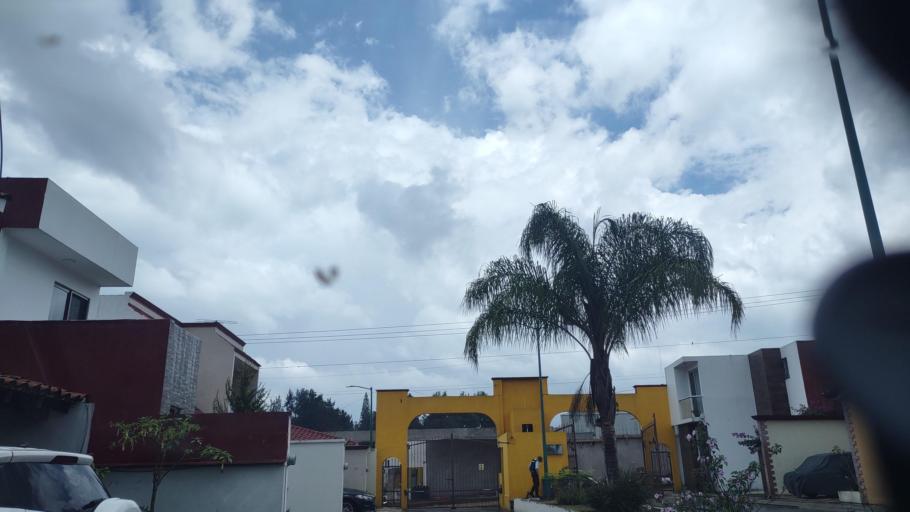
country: MX
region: Veracruz
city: Coatepec
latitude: 19.4511
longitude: -96.9401
